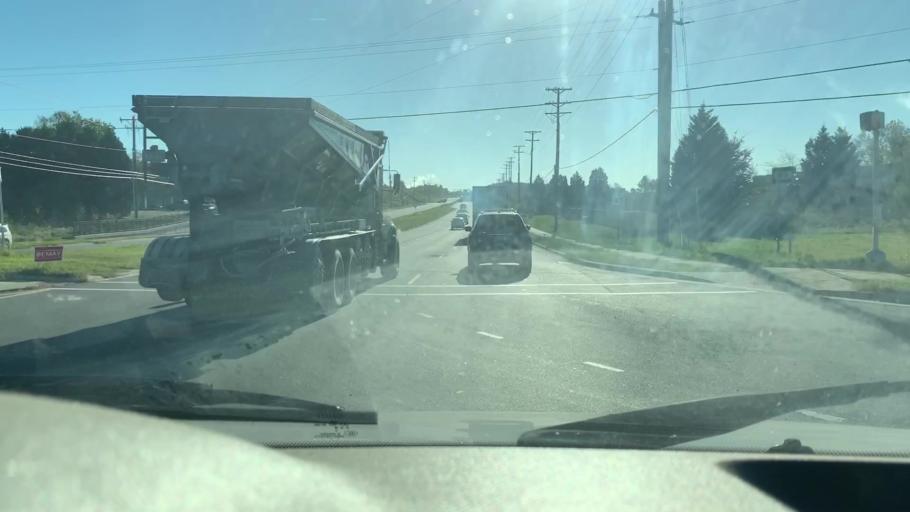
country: US
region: North Carolina
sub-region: Cabarrus County
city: Harrisburg
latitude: 35.4073
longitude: -80.7131
